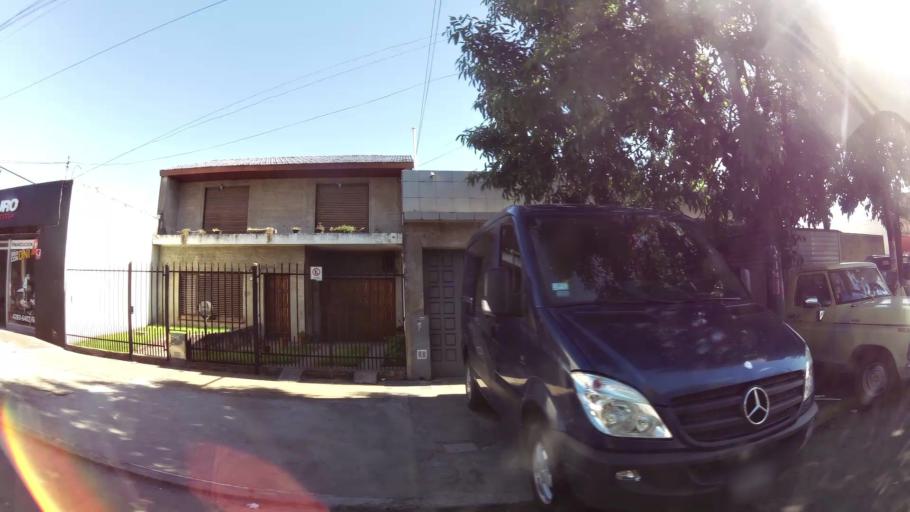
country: AR
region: Buenos Aires
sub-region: Partido de Lomas de Zamora
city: Lomas de Zamora
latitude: -34.7613
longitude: -58.4216
